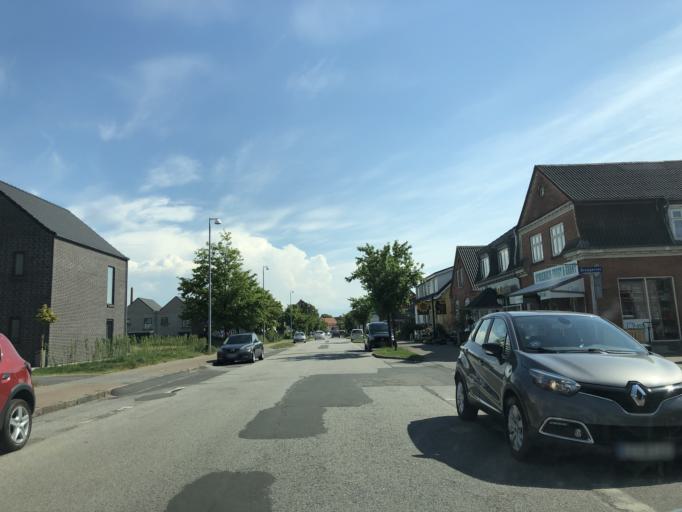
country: DK
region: Central Jutland
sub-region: Holstebro Kommune
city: Holstebro
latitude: 56.3666
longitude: 8.6180
